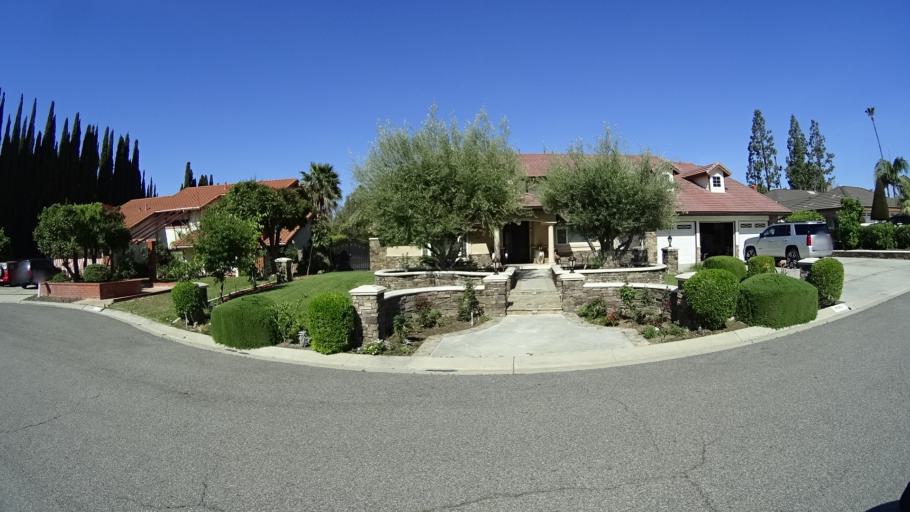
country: US
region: California
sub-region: Orange County
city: Villa Park
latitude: 33.8172
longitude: -117.8148
